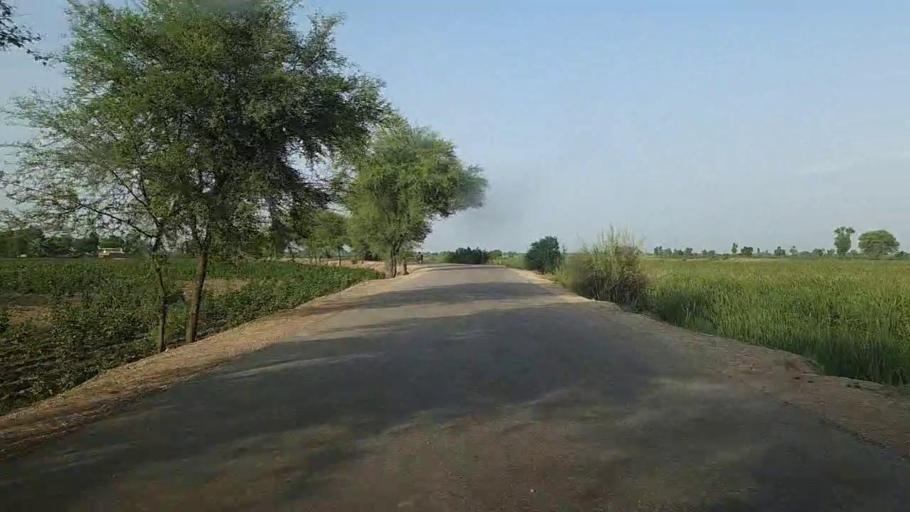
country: PK
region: Sindh
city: Khairpur
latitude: 28.0839
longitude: 69.7986
